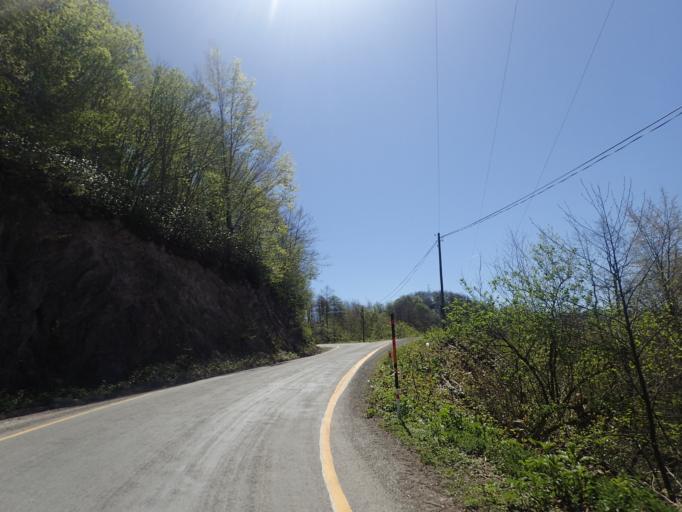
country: TR
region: Ordu
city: Kabaduz
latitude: 40.7940
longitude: 37.9142
